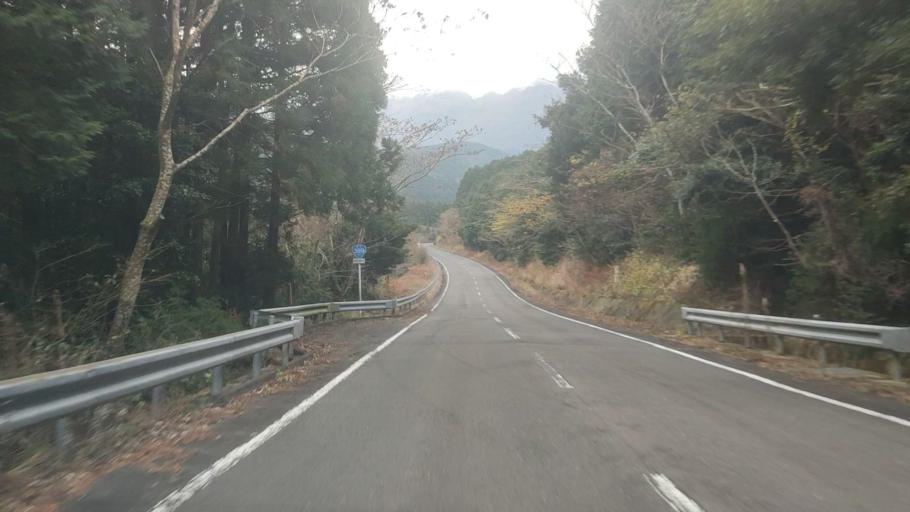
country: JP
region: Nagasaki
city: Shimabara
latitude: 32.7906
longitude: 130.2823
